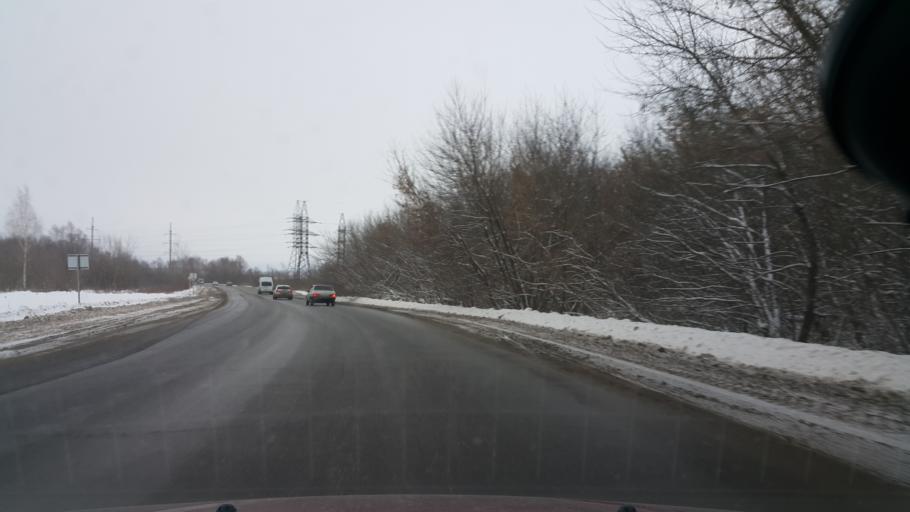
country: RU
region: Tambov
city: Pokrovo-Prigorodnoye
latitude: 52.6554
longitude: 41.4047
